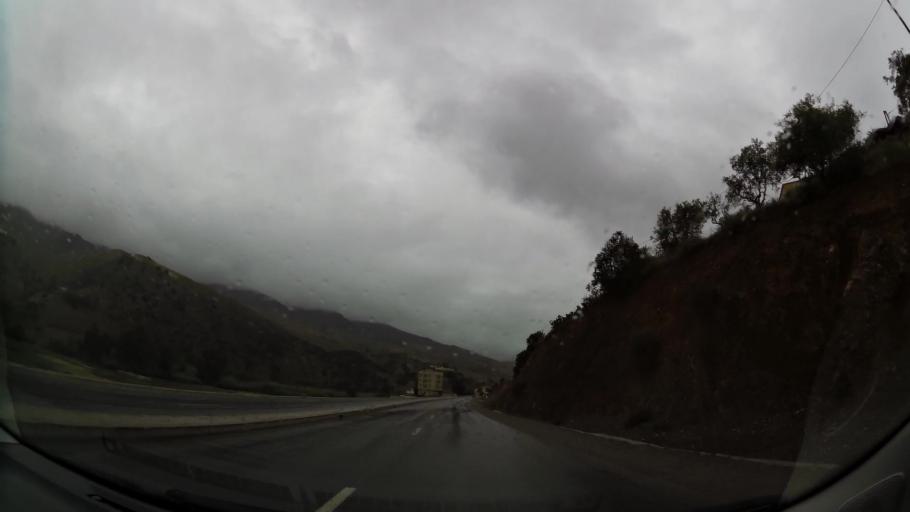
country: MA
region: Taza-Al Hoceima-Taounate
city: Imzourene
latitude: 35.0161
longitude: -3.8190
